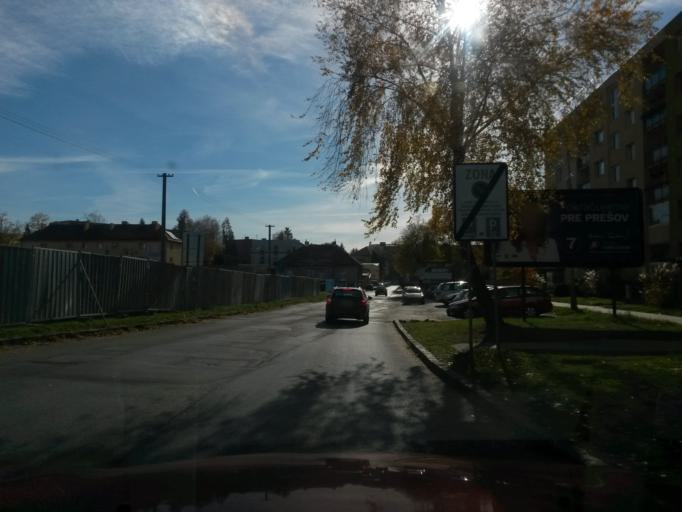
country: SK
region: Presovsky
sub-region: Okres Presov
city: Presov
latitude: 48.9928
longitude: 21.2407
